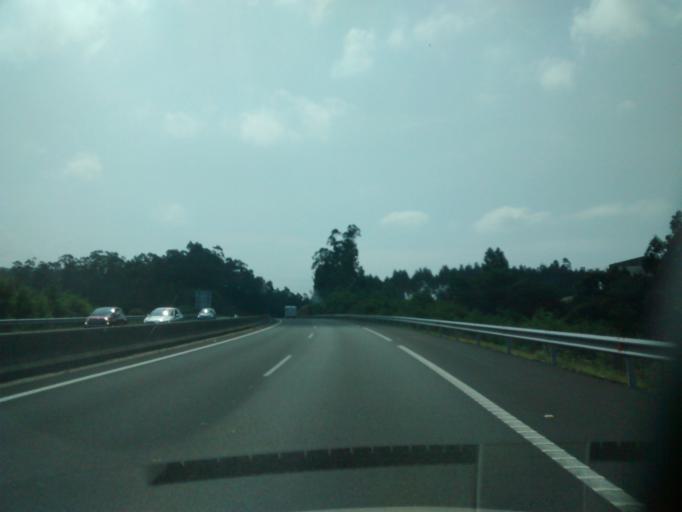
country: ES
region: Galicia
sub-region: Provincia de Pontevedra
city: Barro
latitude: 42.5034
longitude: -8.6562
